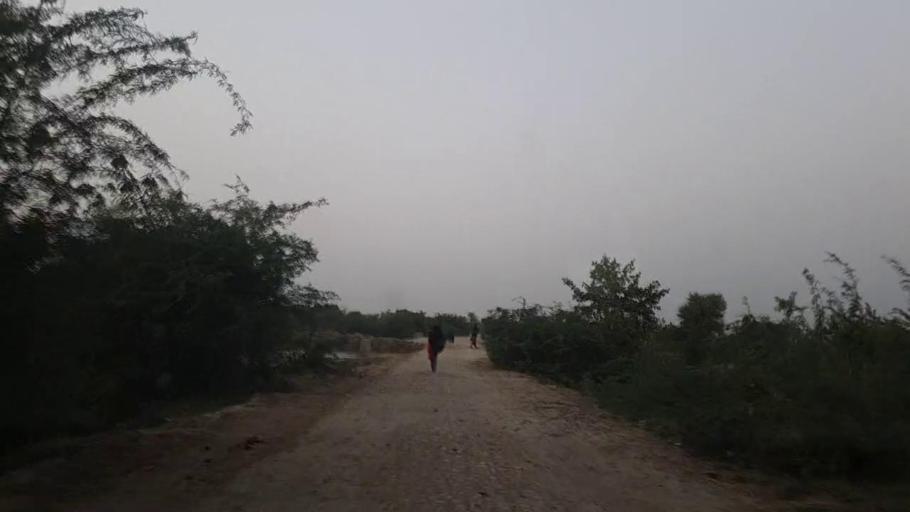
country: PK
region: Sindh
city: Mirpur Sakro
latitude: 24.5855
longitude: 67.7841
